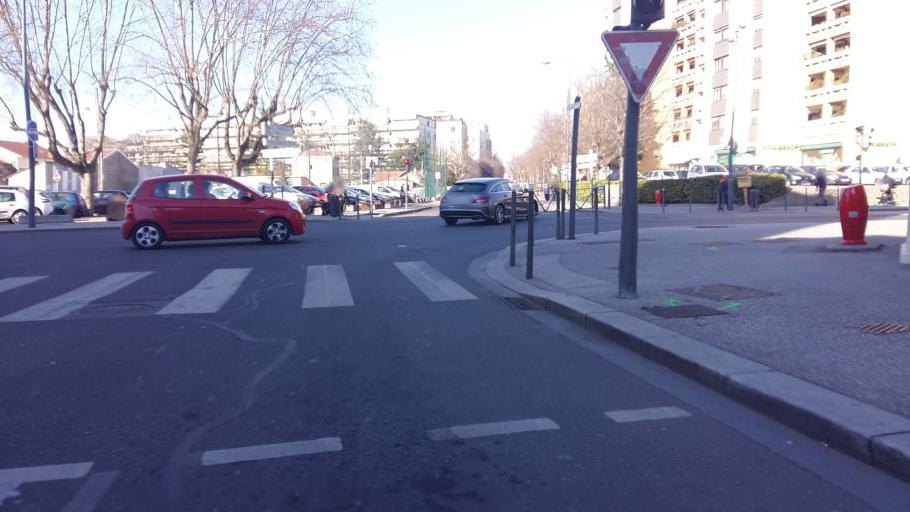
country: FR
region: Rhone-Alpes
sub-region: Departement du Rhone
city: Villeurbanne
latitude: 45.7764
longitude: 4.8740
